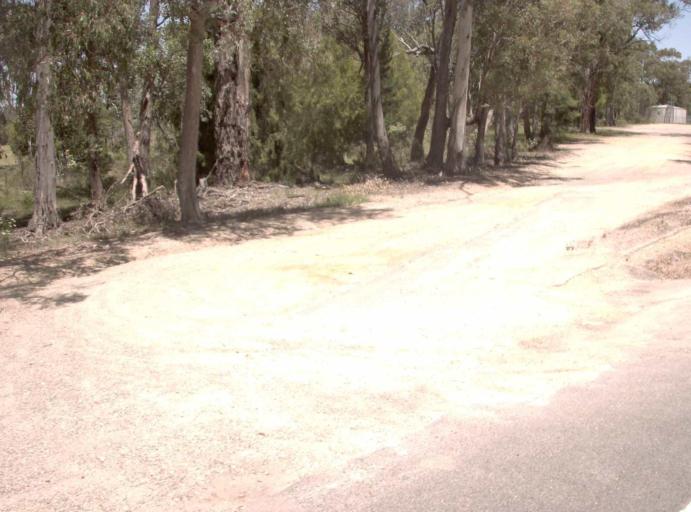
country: AU
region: Victoria
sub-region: East Gippsland
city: Bairnsdale
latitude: -37.7378
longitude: 147.7682
